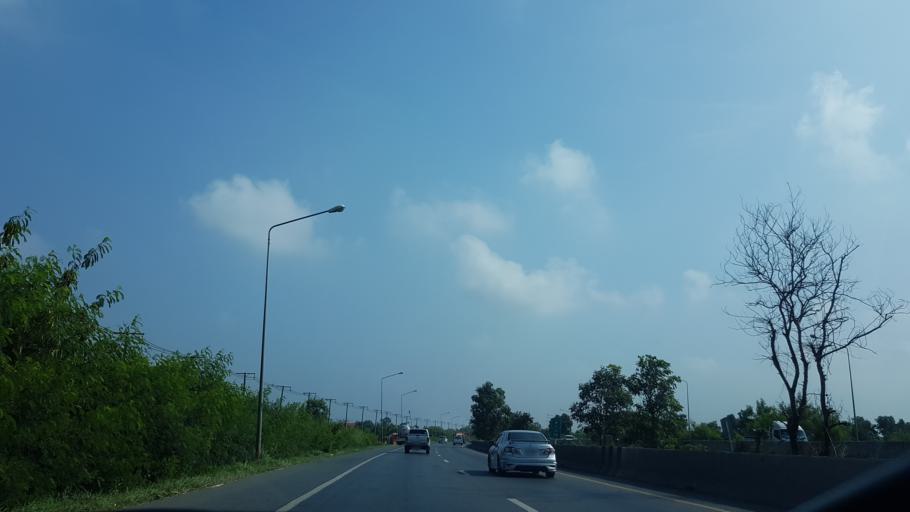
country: TH
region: Pathum Thani
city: Sam Khok
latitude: 14.1400
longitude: 100.5417
